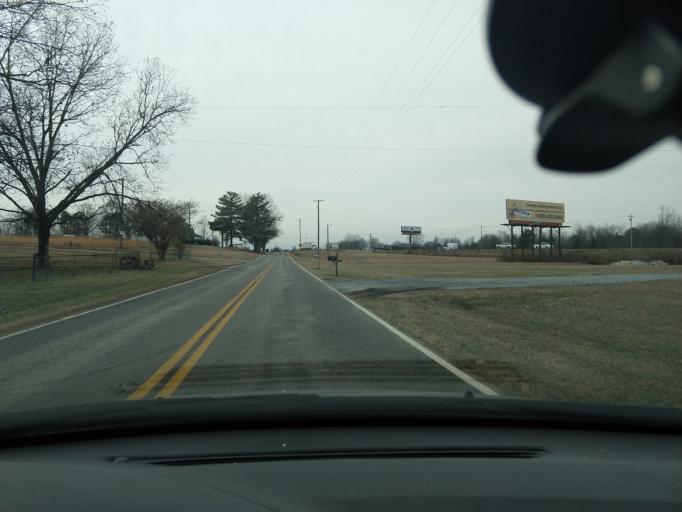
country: US
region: South Carolina
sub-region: Spartanburg County
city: Cowpens
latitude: 35.0652
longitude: -81.7696
